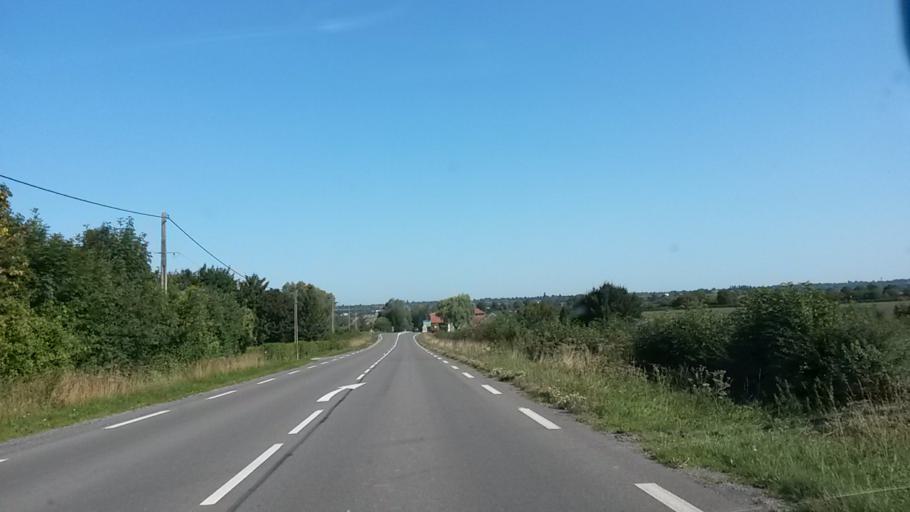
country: FR
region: Picardie
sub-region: Departement de l'Aisne
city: La Flamengrie
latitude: 50.0465
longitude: 3.9271
